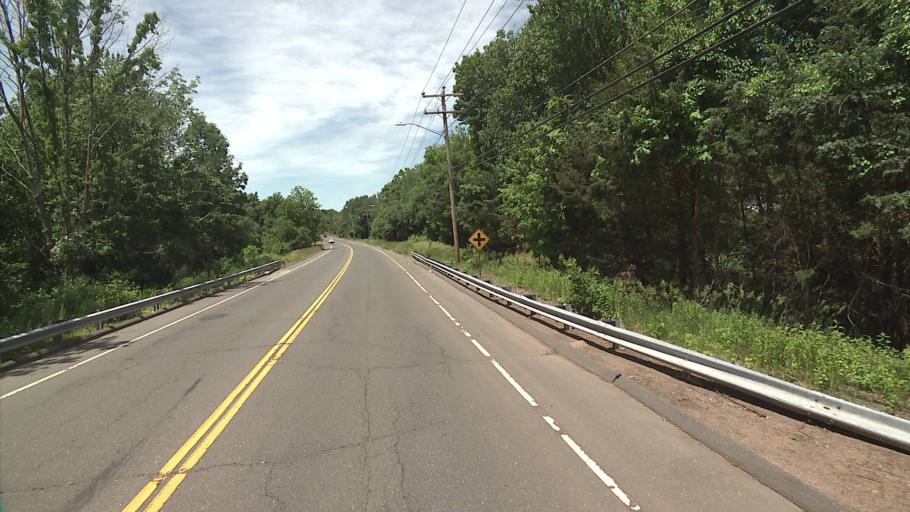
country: US
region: Connecticut
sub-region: New Haven County
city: Meriden
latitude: 41.5972
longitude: -72.8456
